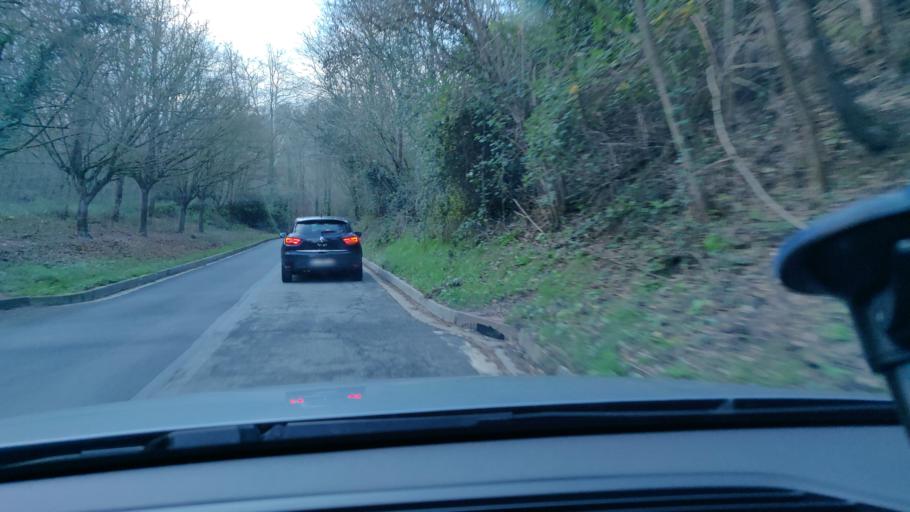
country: FR
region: Midi-Pyrenees
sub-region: Departement de la Haute-Garonne
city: Vieille-Toulouse
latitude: 43.5496
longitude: 1.4463
